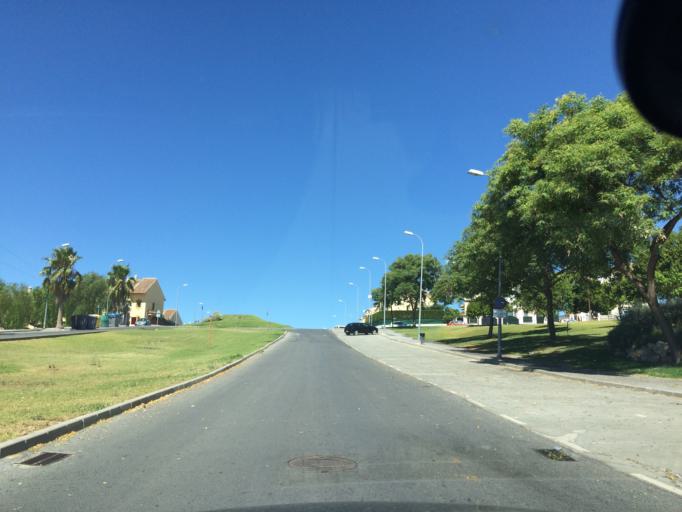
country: ES
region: Andalusia
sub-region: Provincia de Malaga
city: Estacion de Cartama
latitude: 36.7395
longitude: -4.6089
